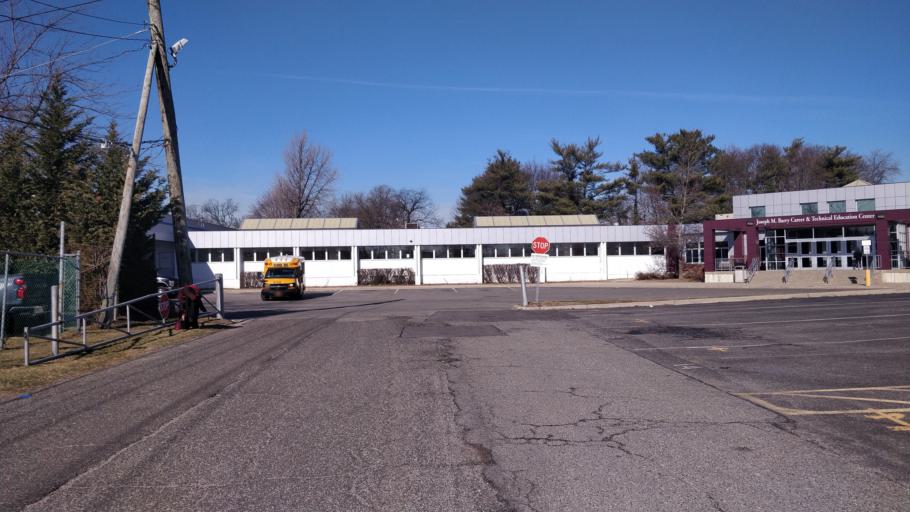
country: US
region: New York
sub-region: Nassau County
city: New Cassel
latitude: 40.7655
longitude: -73.5531
